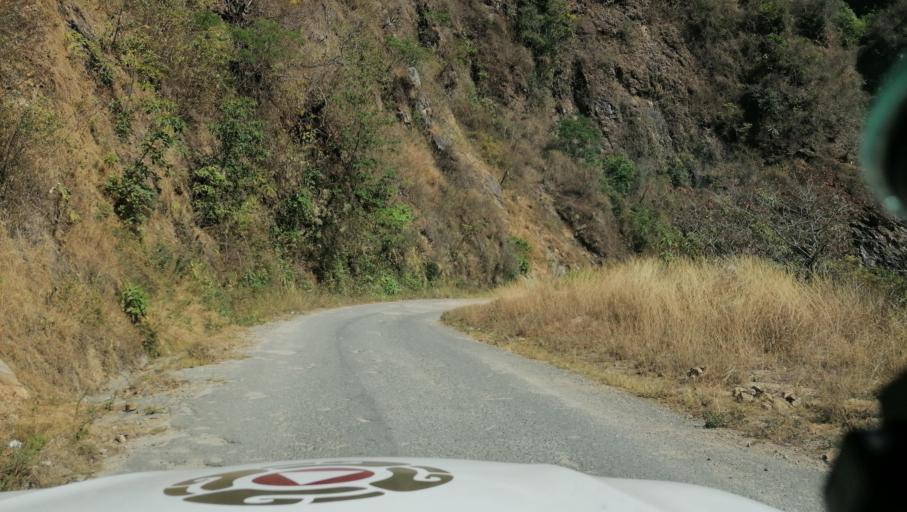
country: MX
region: Chiapas
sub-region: Cacahoatan
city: Benito Juarez
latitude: 15.1841
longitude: -92.1896
